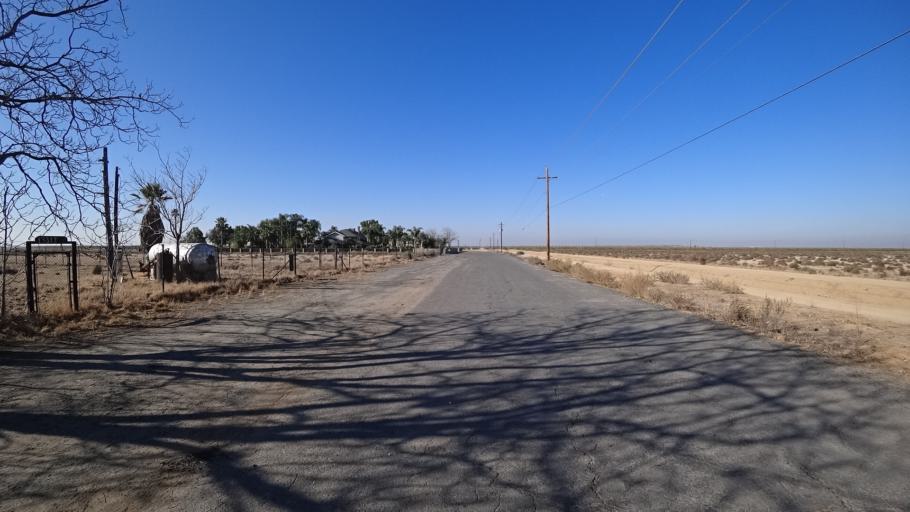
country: US
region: California
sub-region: Kern County
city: Rosedale
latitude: 35.4270
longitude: -119.1500
